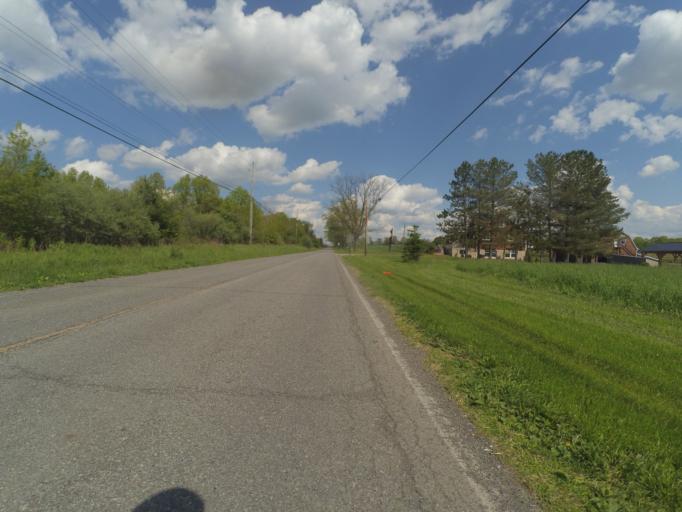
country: US
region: Ohio
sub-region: Trumbull County
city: Mineral Ridge
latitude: 41.1340
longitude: -80.7441
